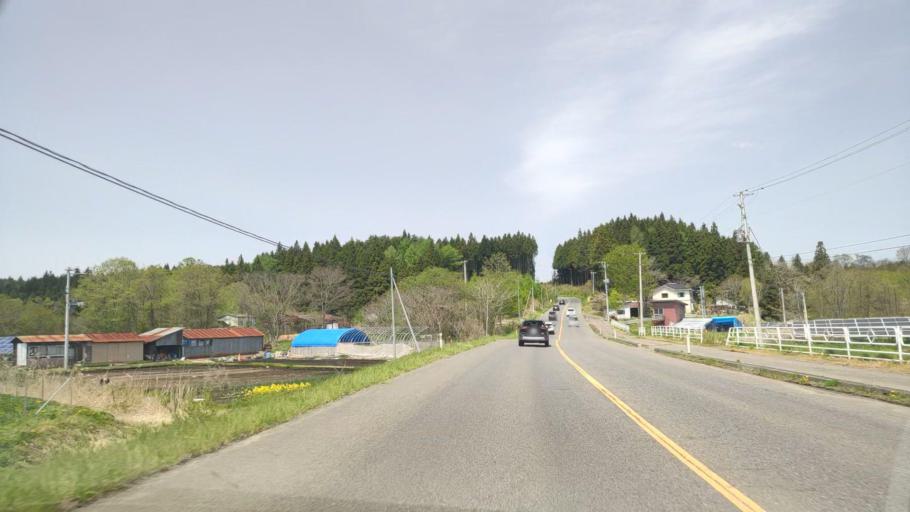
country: JP
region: Aomori
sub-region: Misawa Shi
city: Inuotose
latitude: 40.5631
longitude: 141.3820
